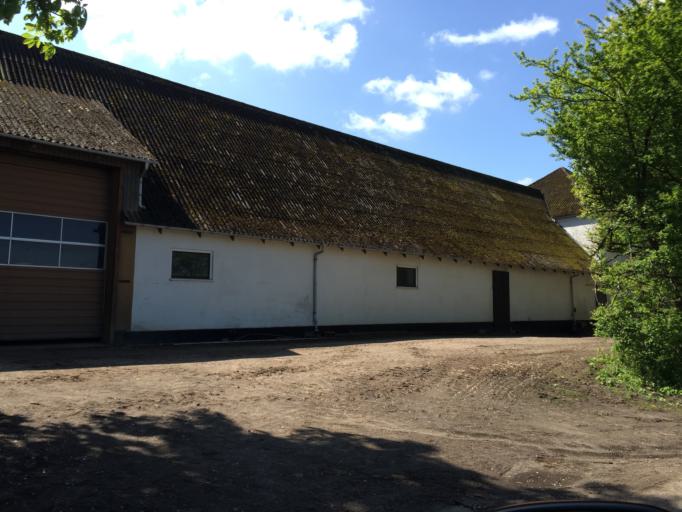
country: DK
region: South Denmark
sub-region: Middelfart Kommune
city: Brenderup
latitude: 55.5122
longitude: 9.9874
